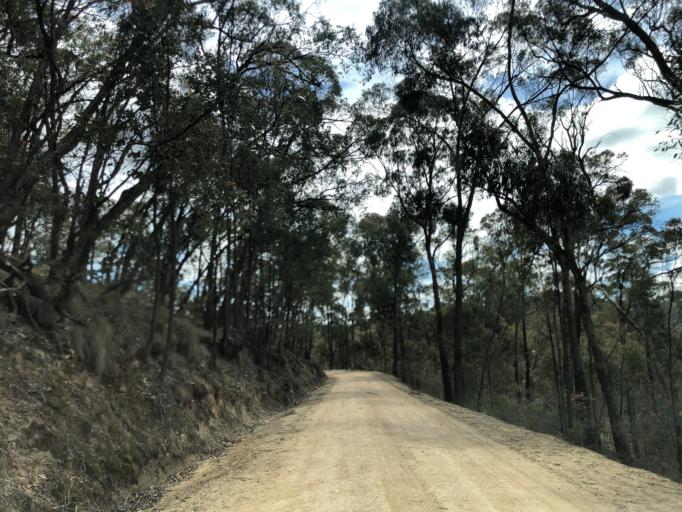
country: AU
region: Victoria
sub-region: Benalla
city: Benalla
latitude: -36.7557
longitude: 146.1689
